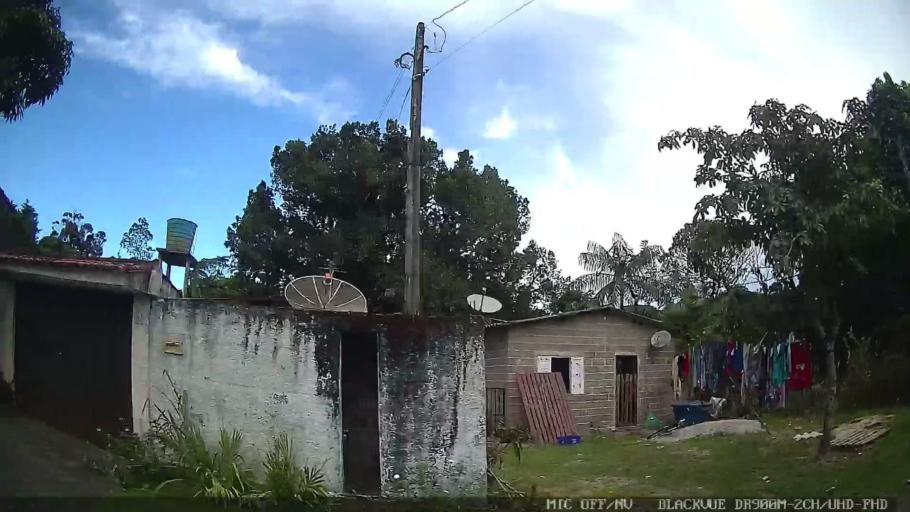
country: BR
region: Sao Paulo
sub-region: Iguape
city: Iguape
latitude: -24.6918
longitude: -47.5282
